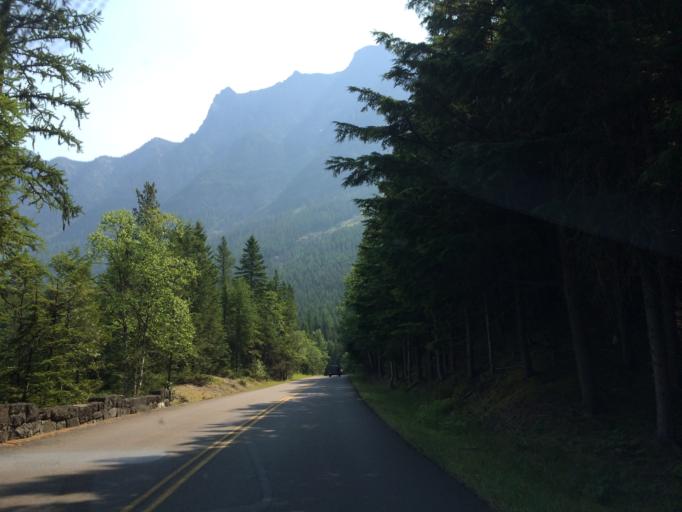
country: US
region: Montana
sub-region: Flathead County
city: Columbia Falls
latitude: 48.6418
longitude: -113.8547
